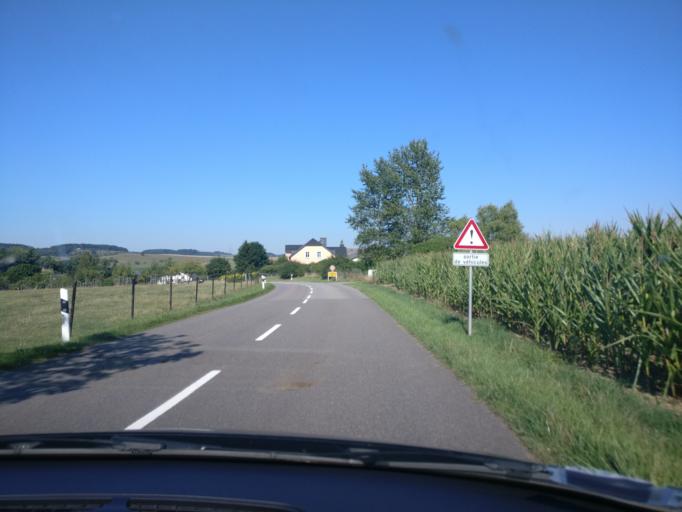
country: LU
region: Grevenmacher
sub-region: Canton d'Echternach
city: Bech
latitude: 49.7260
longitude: 6.3382
